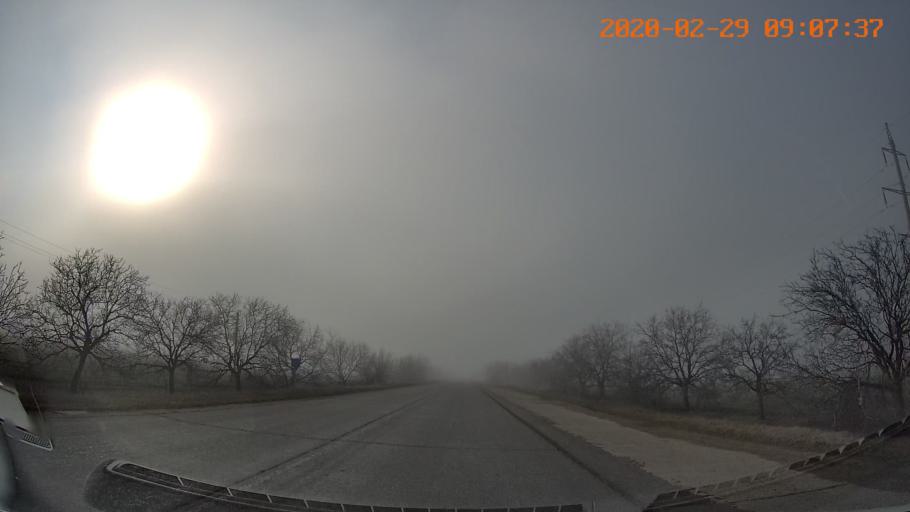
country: MD
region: Telenesti
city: Tiraspolul Nou
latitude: 46.8602
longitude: 29.7495
